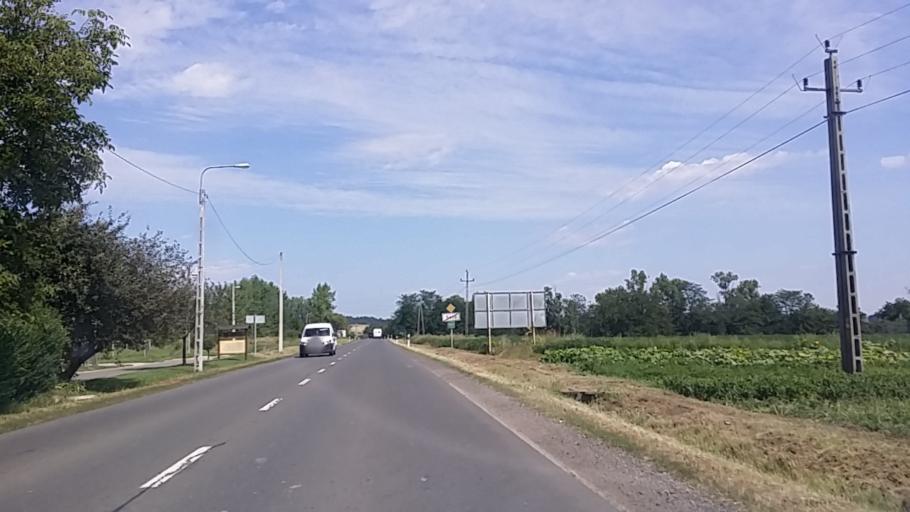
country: HU
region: Baranya
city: Sasd
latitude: 46.2651
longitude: 18.1045
